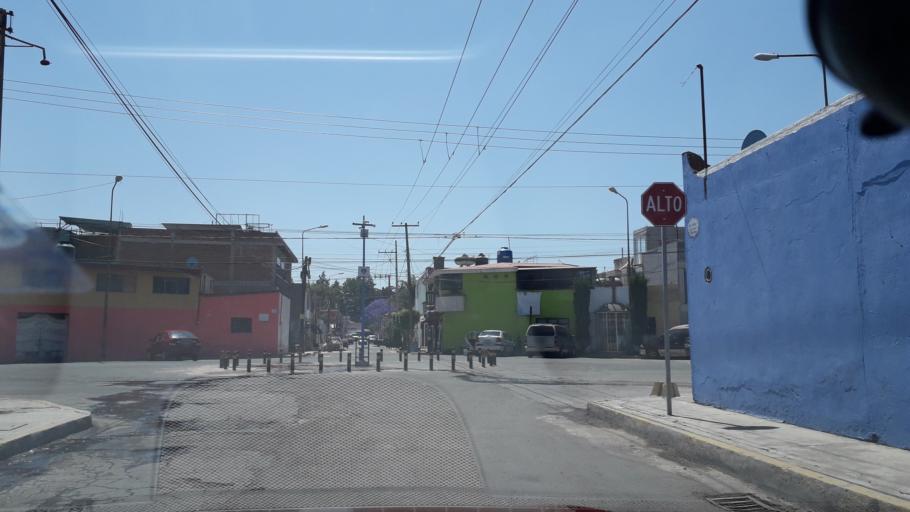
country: MX
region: Puebla
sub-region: Cuautlancingo
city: Sanctorum
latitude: 19.0925
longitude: -98.2370
